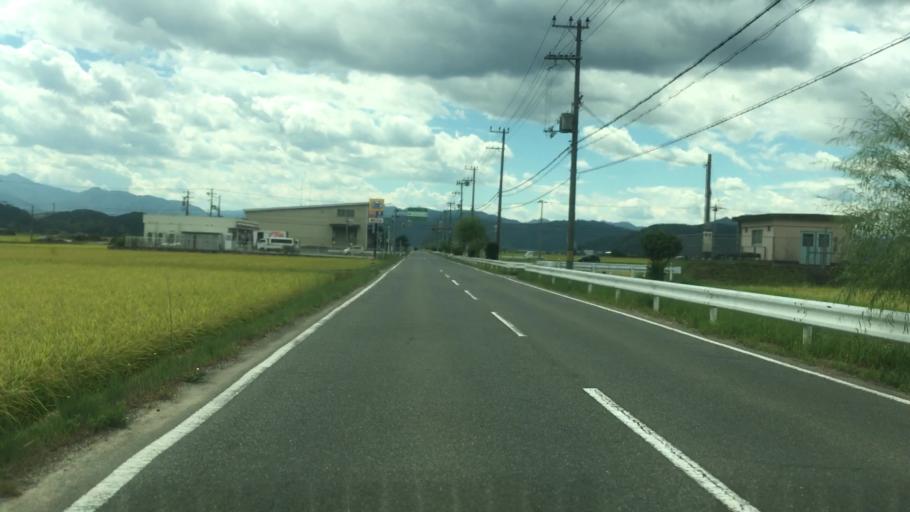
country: JP
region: Hyogo
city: Toyooka
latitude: 35.5261
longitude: 134.8398
